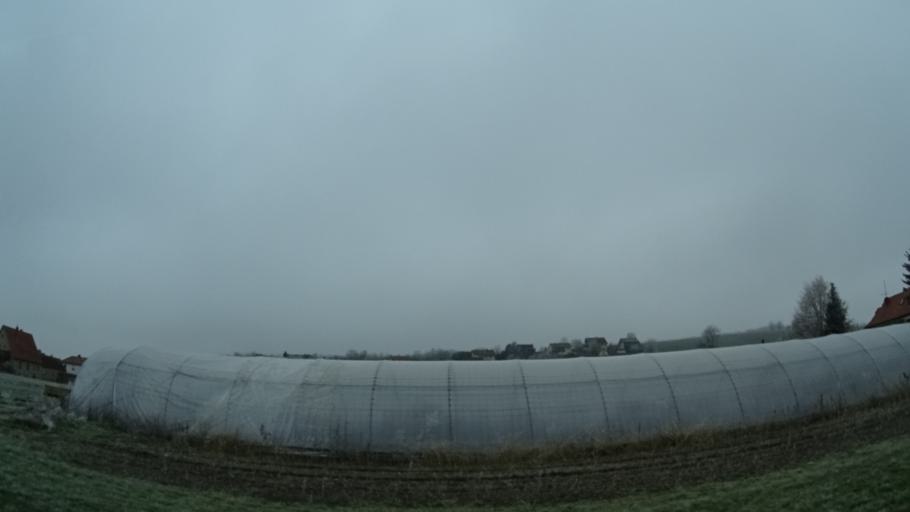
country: DE
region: Bavaria
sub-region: Regierungsbezirk Unterfranken
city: Segnitz
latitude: 49.6768
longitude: 10.1433
